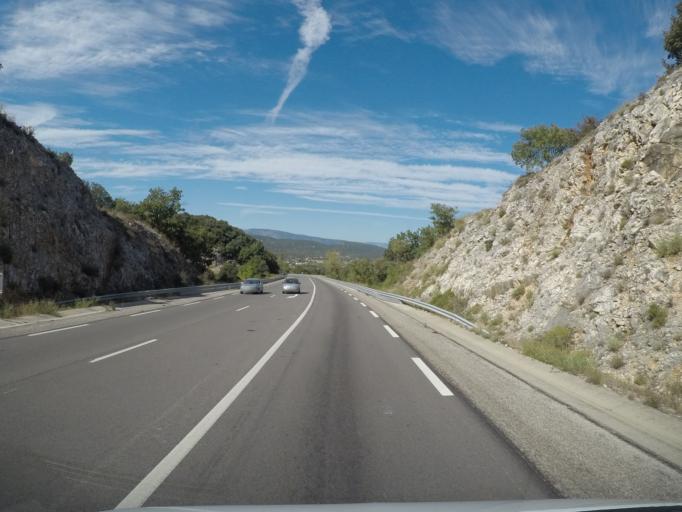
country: FR
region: Languedoc-Roussillon
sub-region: Departement de l'Herault
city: Saint-Martin-de-Londres
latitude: 43.7723
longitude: 3.7457
